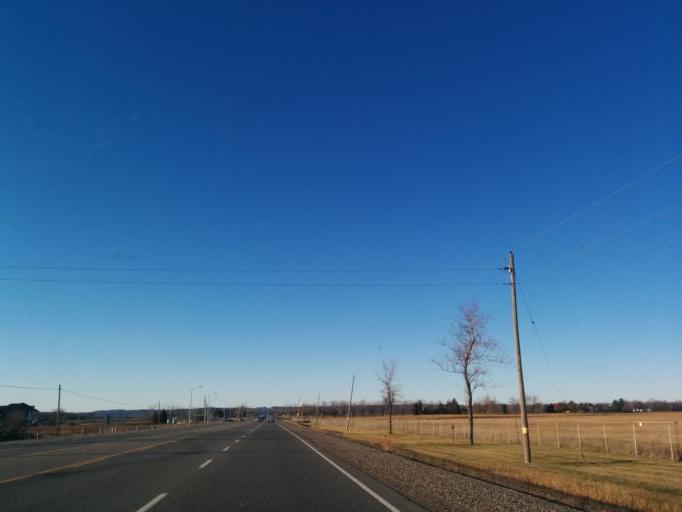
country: CA
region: Ontario
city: Brampton
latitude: 43.7836
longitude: -79.8917
